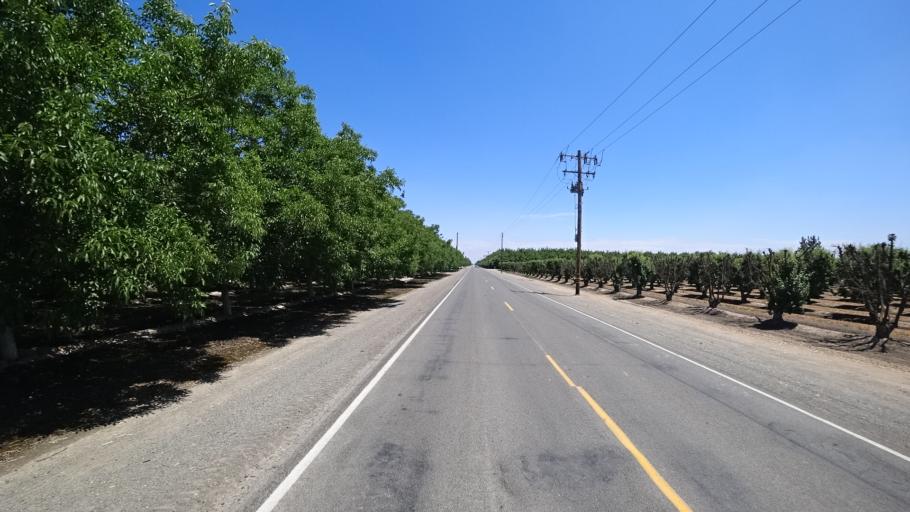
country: US
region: California
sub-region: Kings County
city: Lucerne
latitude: 36.4013
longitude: -119.6174
